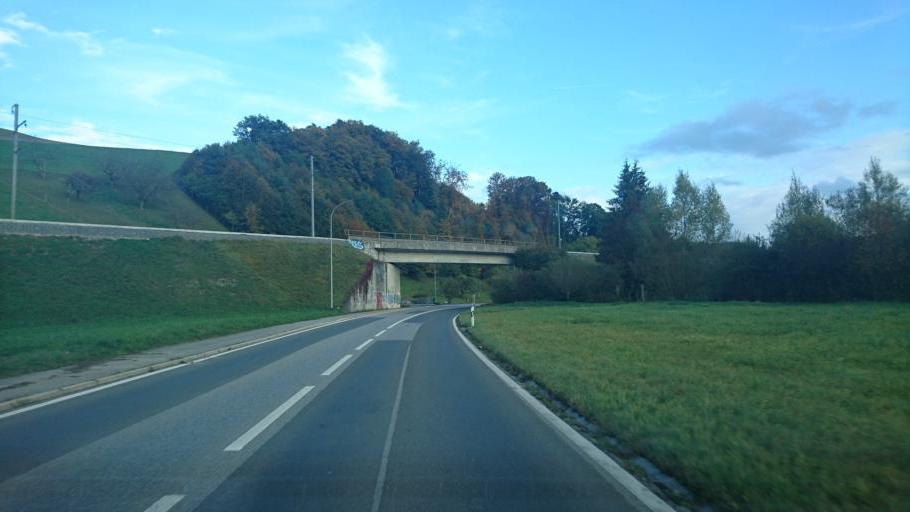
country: CH
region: Bern
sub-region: Bern-Mittelland District
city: Biglen
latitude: 46.9319
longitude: 7.6169
